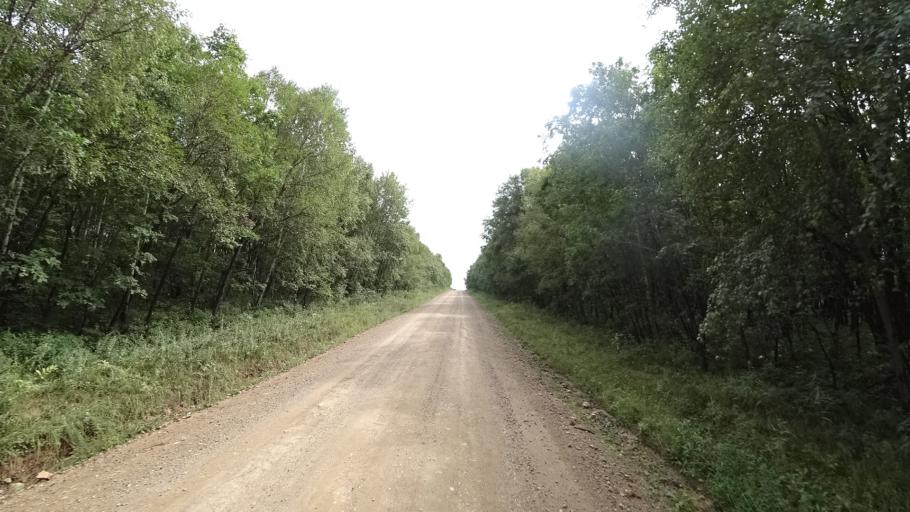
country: RU
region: Primorskiy
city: Lyalichi
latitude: 44.0954
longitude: 132.4310
